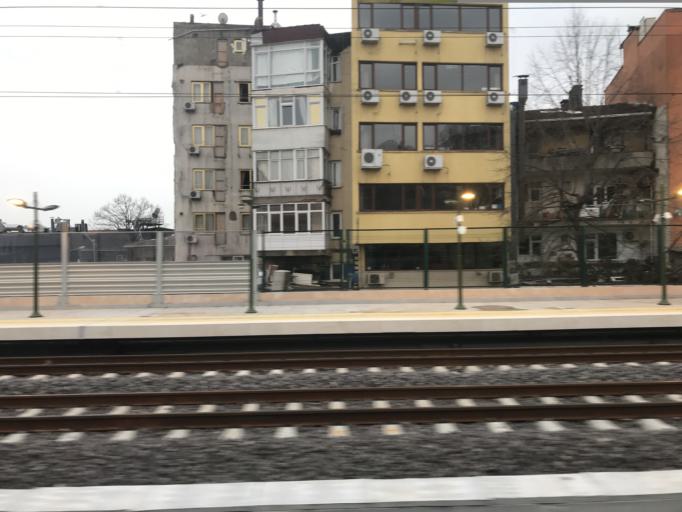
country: TR
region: Istanbul
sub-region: Atasehir
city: Atasehir
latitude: 40.9531
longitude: 29.0972
